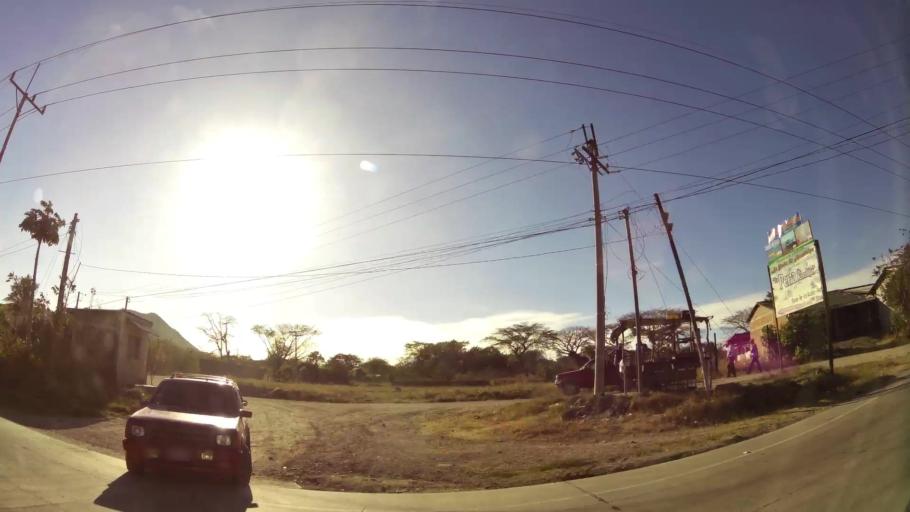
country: SV
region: Santa Ana
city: Metapan
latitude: 14.2886
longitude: -89.4622
